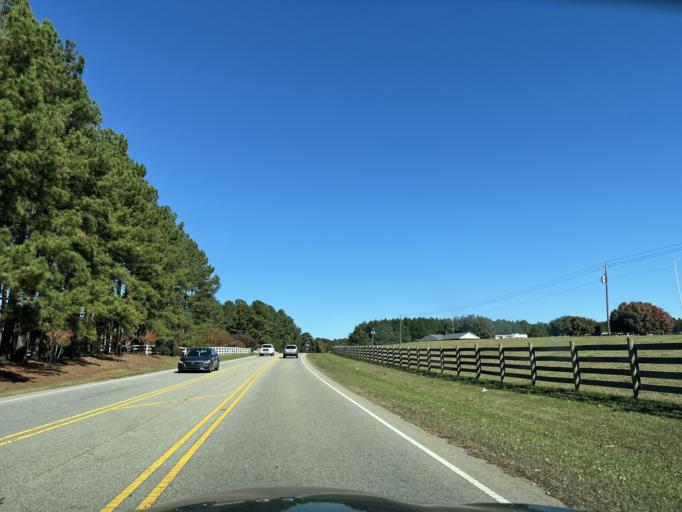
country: US
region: North Carolina
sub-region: Wake County
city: Garner
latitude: 35.6754
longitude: -78.7038
